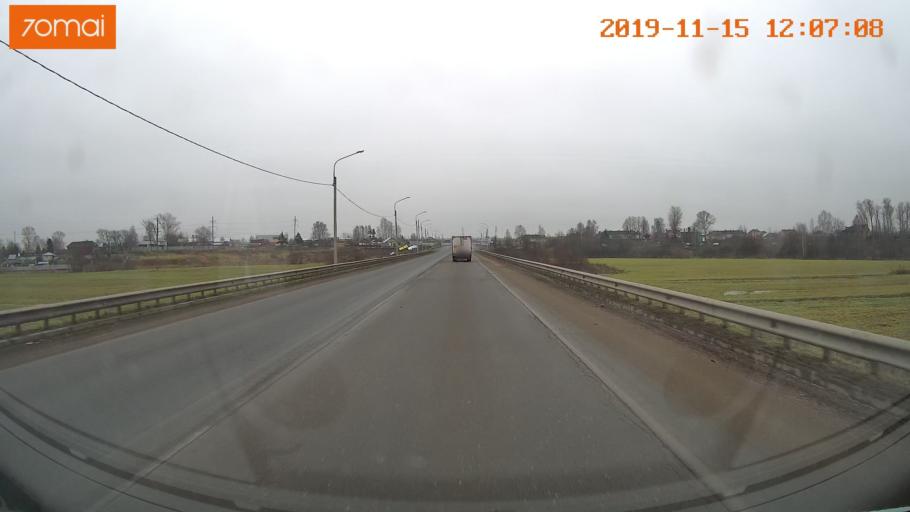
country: RU
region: Vologda
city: Molochnoye
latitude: 59.2362
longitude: 39.7717
